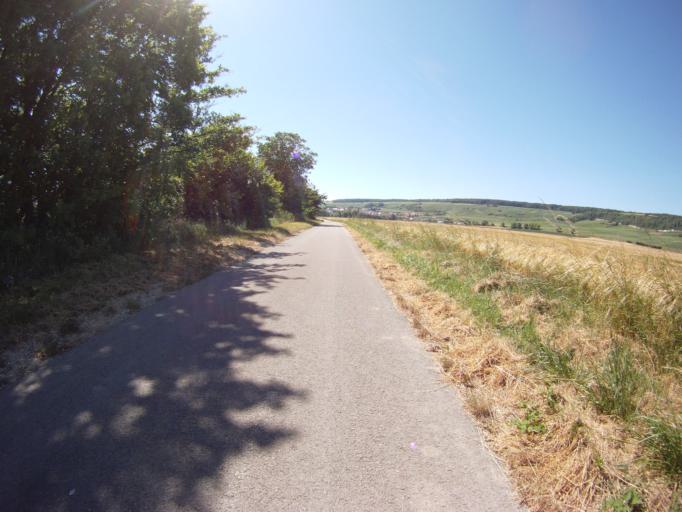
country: FR
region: Champagne-Ardenne
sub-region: Departement de la Marne
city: Dormans
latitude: 49.0893
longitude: 3.6616
